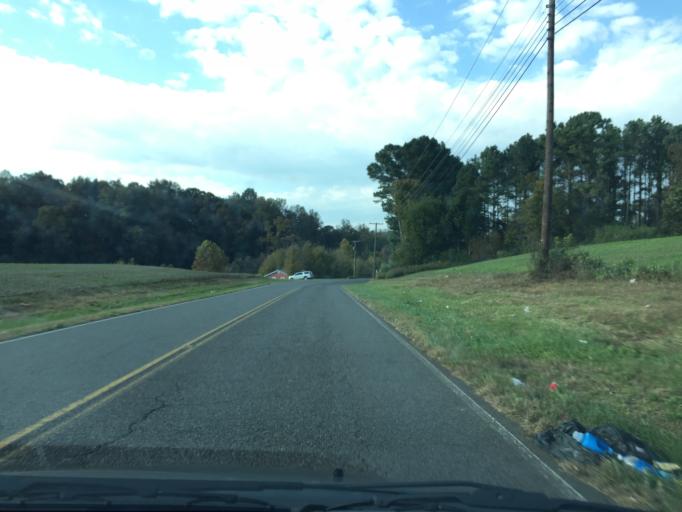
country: US
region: Tennessee
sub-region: Loudon County
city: Loudon
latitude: 35.7149
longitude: -84.3458
